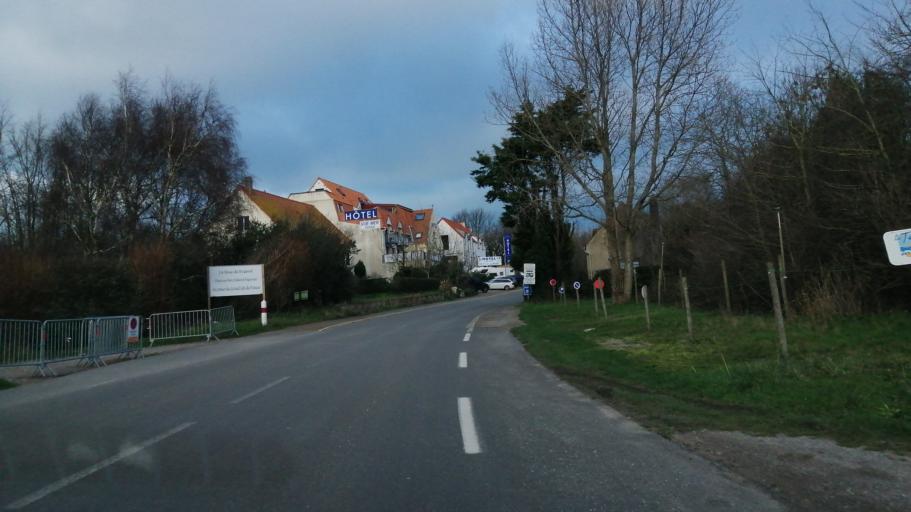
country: FR
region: Nord-Pas-de-Calais
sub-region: Departement du Pas-de-Calais
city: Wissant
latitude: 50.8800
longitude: 1.6576
